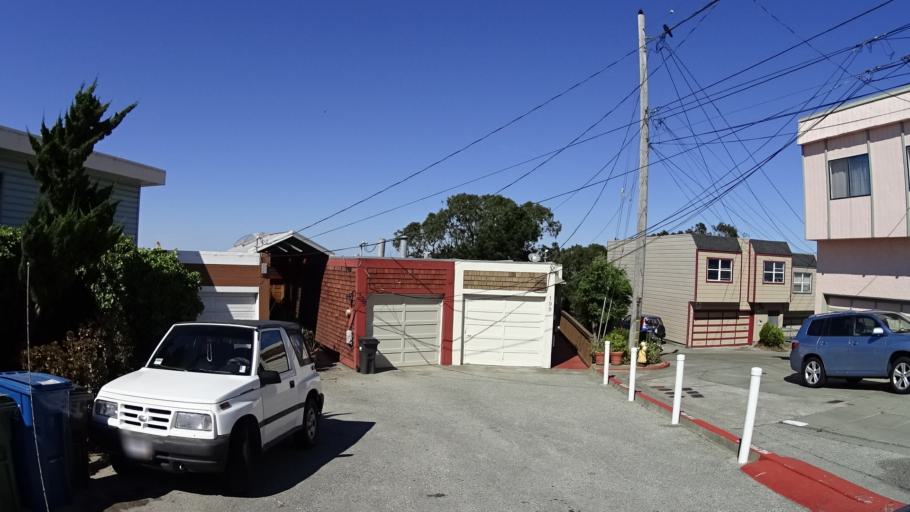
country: US
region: California
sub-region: San Mateo County
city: Daly City
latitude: 37.7082
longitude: -122.4640
